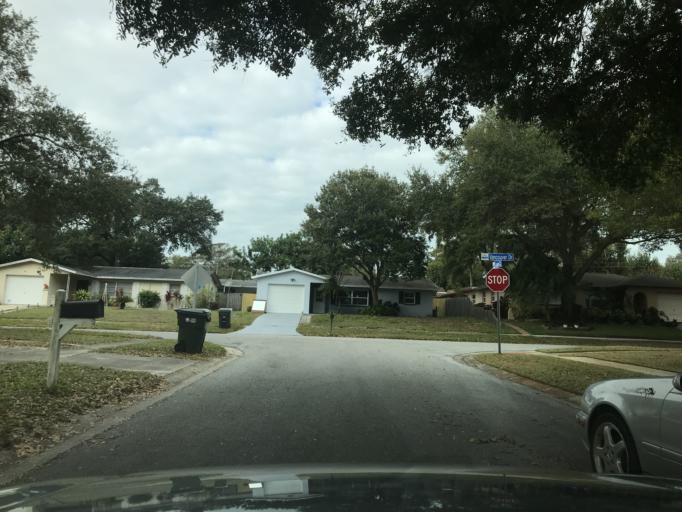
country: US
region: Florida
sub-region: Pinellas County
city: Largo
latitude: 27.9304
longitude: -82.7798
